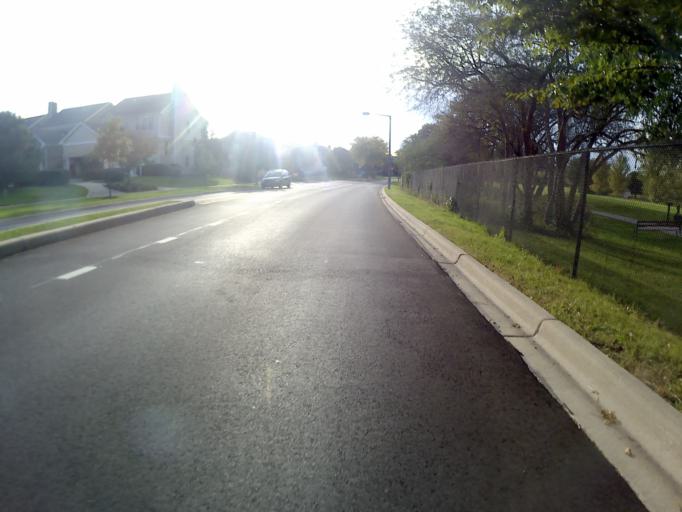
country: US
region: Illinois
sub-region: DuPage County
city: Lisle
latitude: 41.7770
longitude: -88.0734
